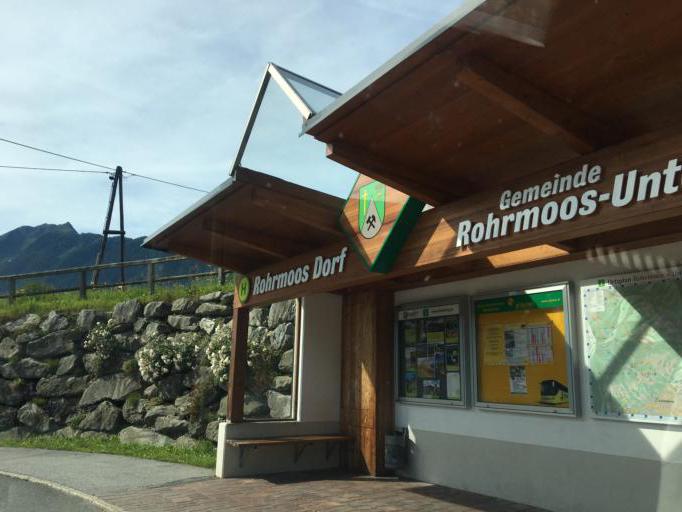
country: AT
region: Styria
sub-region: Politischer Bezirk Liezen
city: Schladming
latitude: 47.3831
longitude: 13.6726
